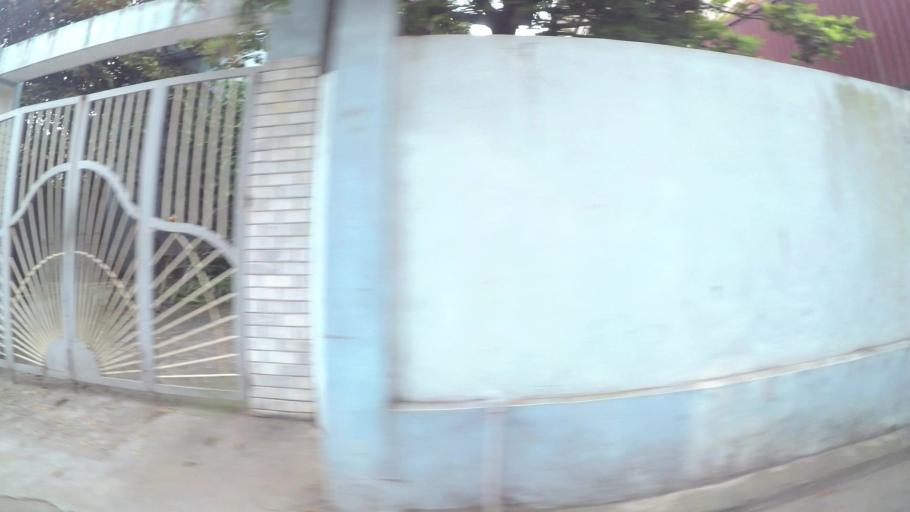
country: VN
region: Ha Noi
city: Trau Quy
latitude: 21.0698
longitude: 105.9198
